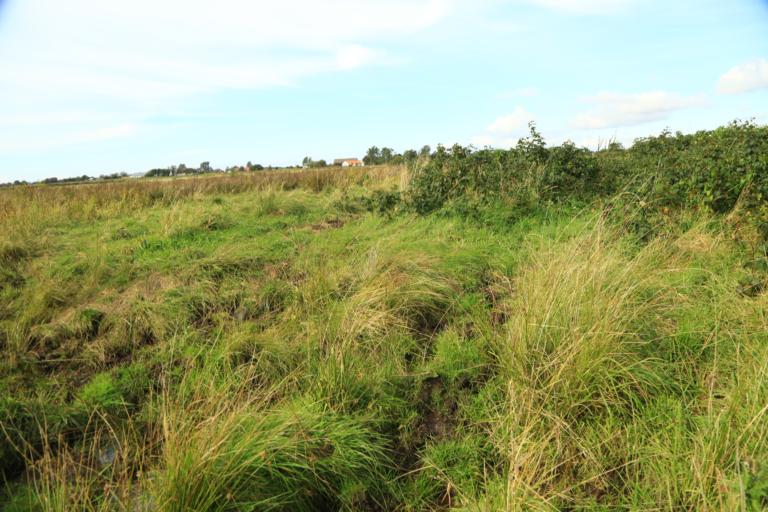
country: SE
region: Halland
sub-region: Varbergs Kommun
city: Traslovslage
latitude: 57.0240
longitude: 12.3332
